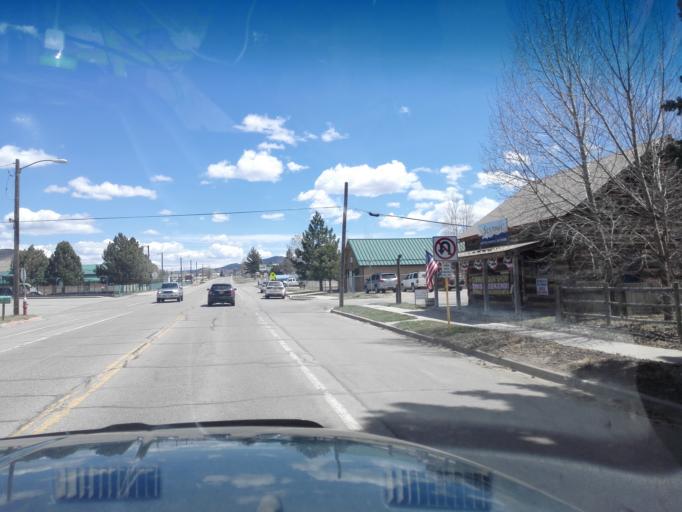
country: US
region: Colorado
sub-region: Custer County
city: Westcliffe
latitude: 38.1359
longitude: -105.4632
